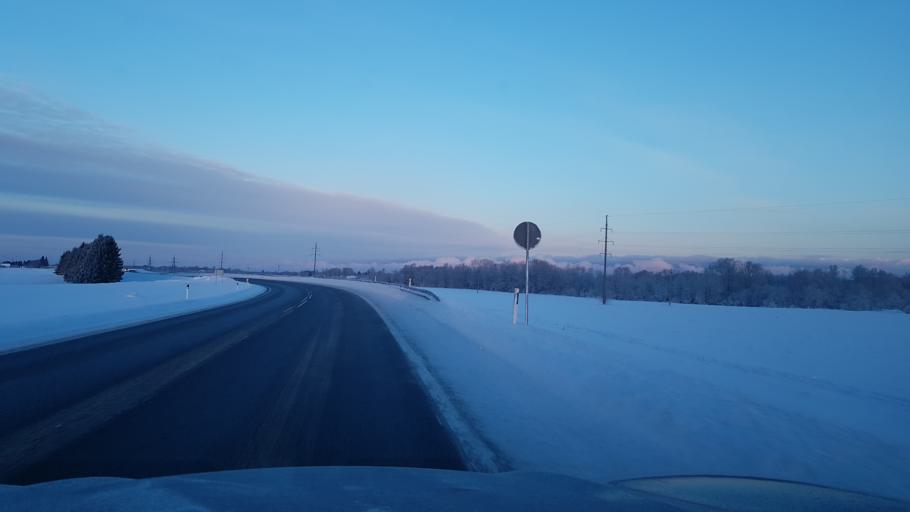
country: EE
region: Ida-Virumaa
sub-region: Narva-Joesuu linn
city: Narva-Joesuu
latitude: 59.4037
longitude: 28.0522
